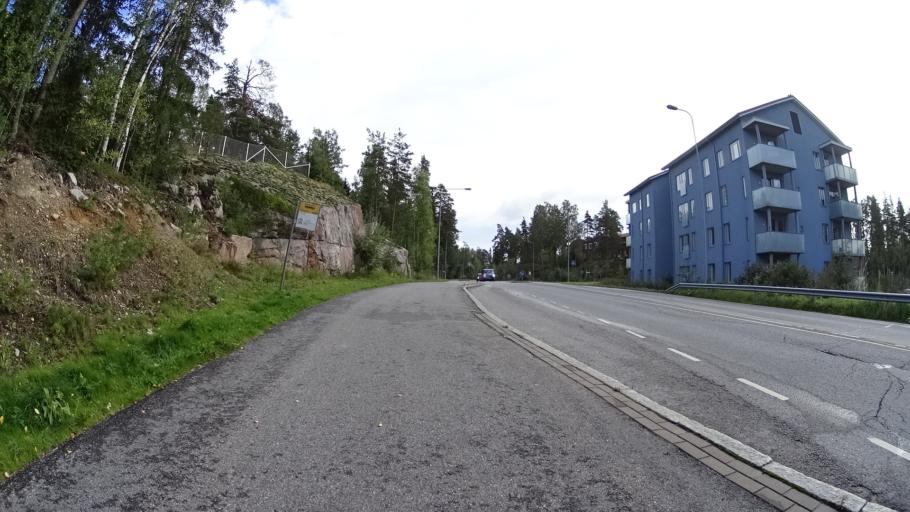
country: FI
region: Uusimaa
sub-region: Helsinki
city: Espoo
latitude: 60.2281
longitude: 24.6667
